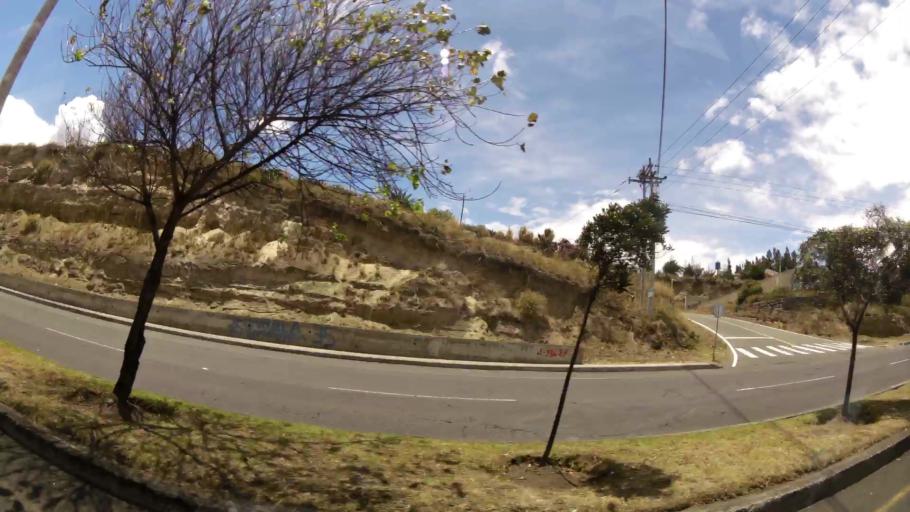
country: EC
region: Tungurahua
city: Pelileo
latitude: -1.3094
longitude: -78.5995
